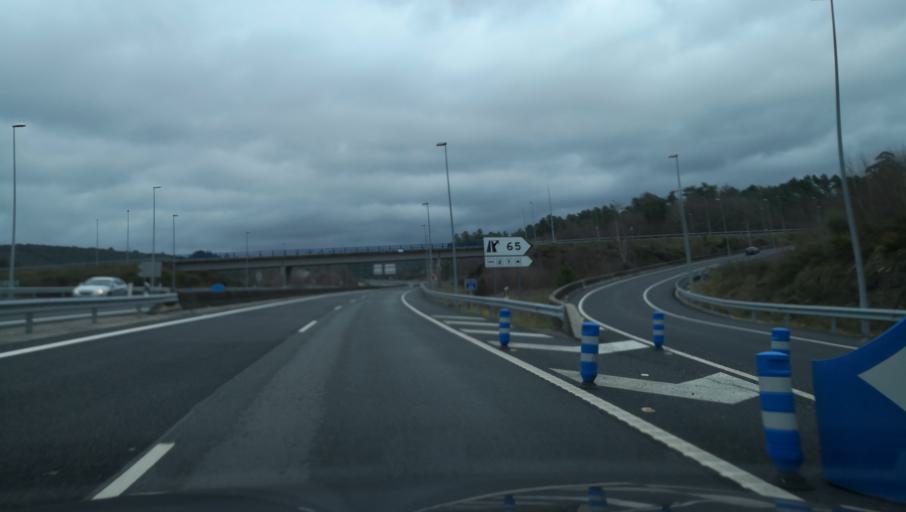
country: ES
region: Galicia
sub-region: Provincia de Ourense
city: Pinor
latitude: 42.5224
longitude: -8.0187
